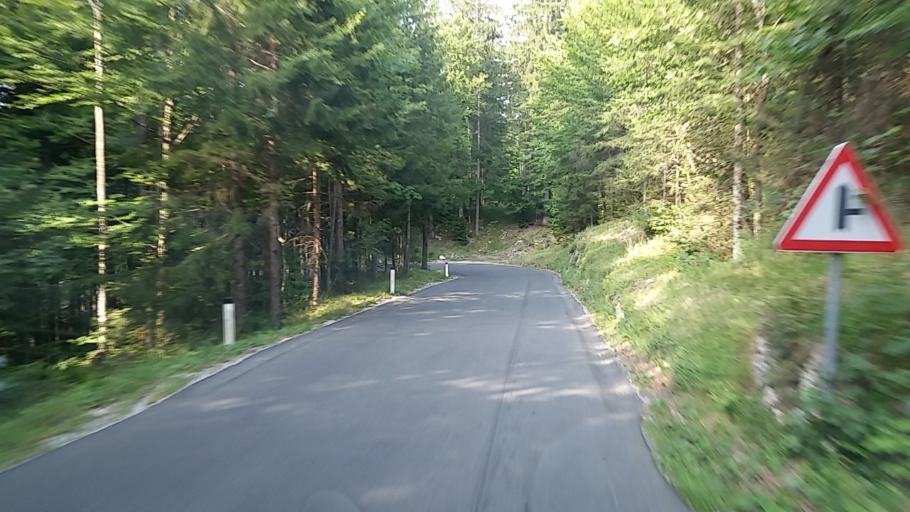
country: SI
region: Bohinj
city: Bohinjska Bistrica
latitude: 46.2732
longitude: 14.0220
